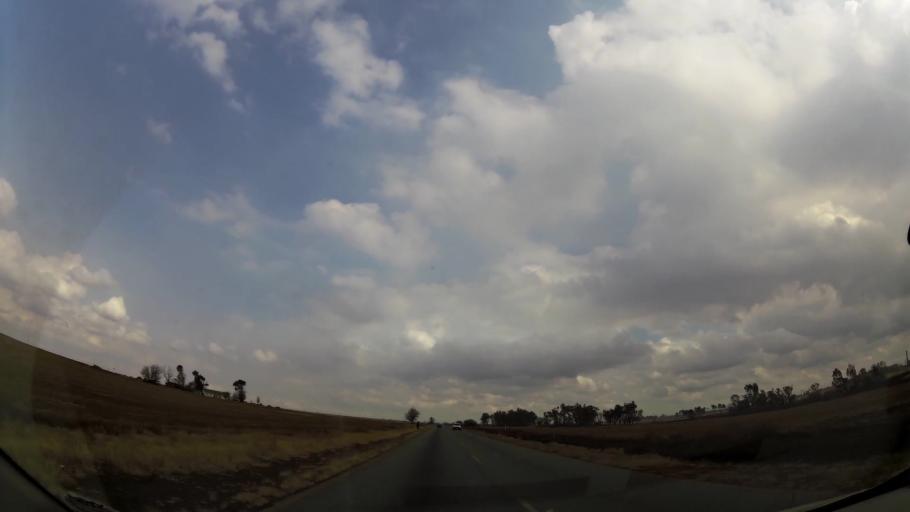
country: ZA
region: Orange Free State
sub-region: Fezile Dabi District Municipality
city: Sasolburg
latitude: -26.8291
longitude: 27.8997
